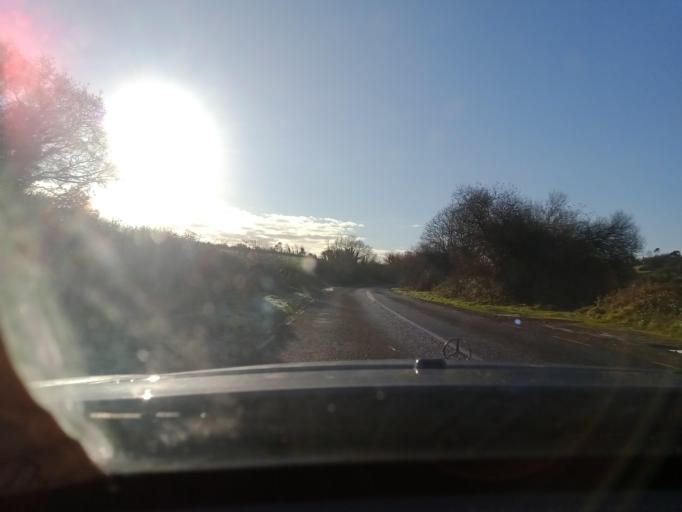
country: IE
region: Leinster
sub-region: Kilkenny
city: Graiguenamanagh
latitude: 52.5832
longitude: -6.9479
